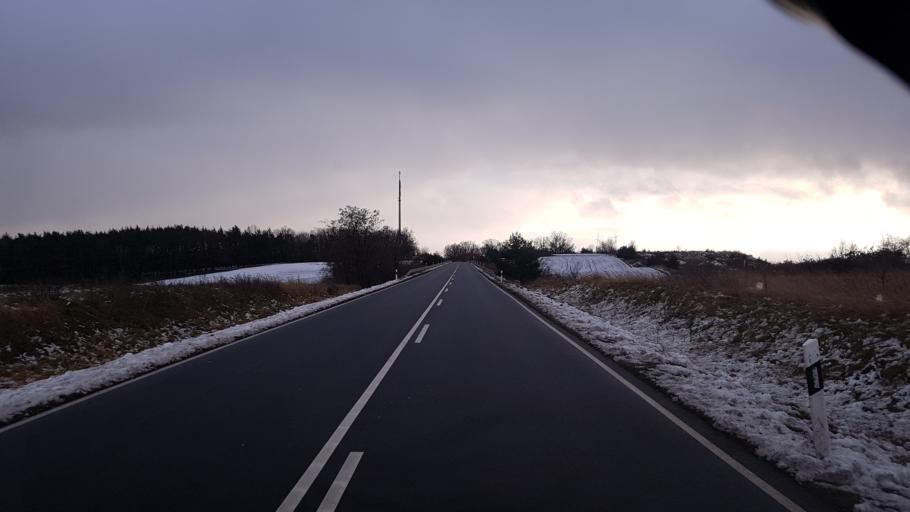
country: DE
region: Brandenburg
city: Heinersbruck
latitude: 51.8445
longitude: 14.5857
